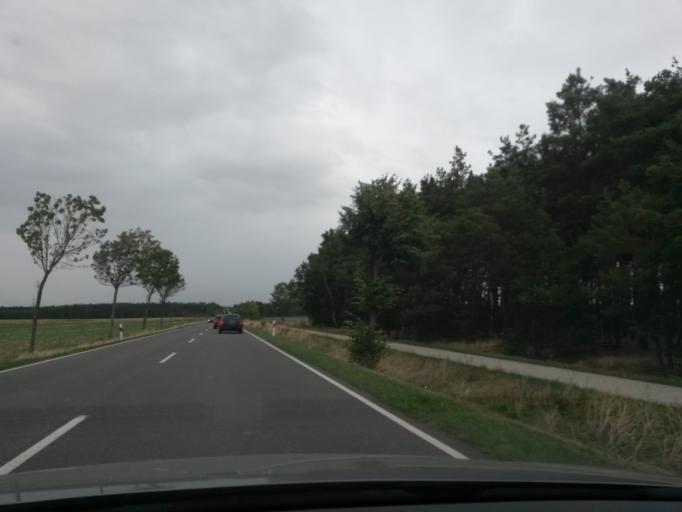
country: DE
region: Saxony-Anhalt
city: Klietz
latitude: 52.7087
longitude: 12.0686
